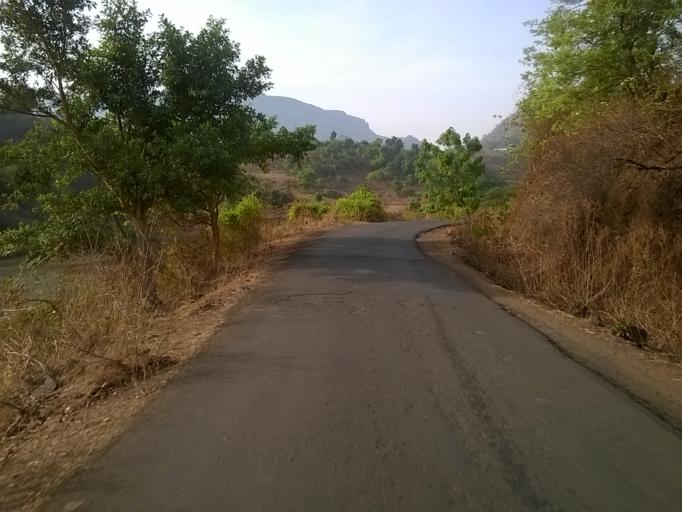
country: IN
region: Maharashtra
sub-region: Raigarh
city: Matheran
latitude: 19.0280
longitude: 73.2429
